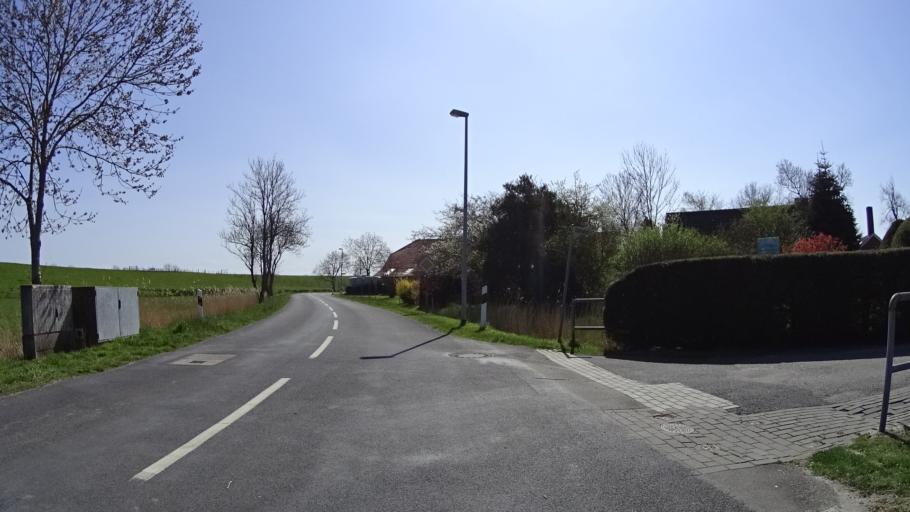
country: DE
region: Lower Saxony
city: Weener
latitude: 53.1901
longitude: 7.4017
